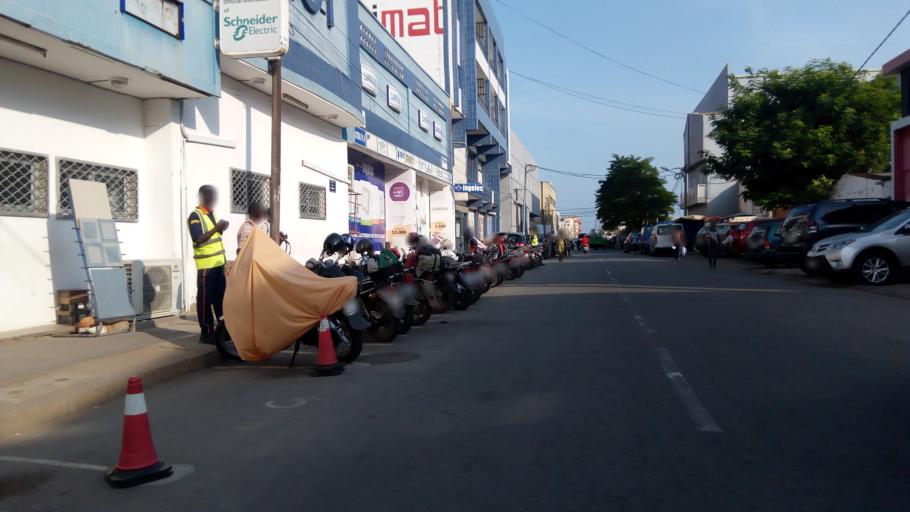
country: TG
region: Maritime
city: Lome
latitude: 6.1279
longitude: 1.2217
